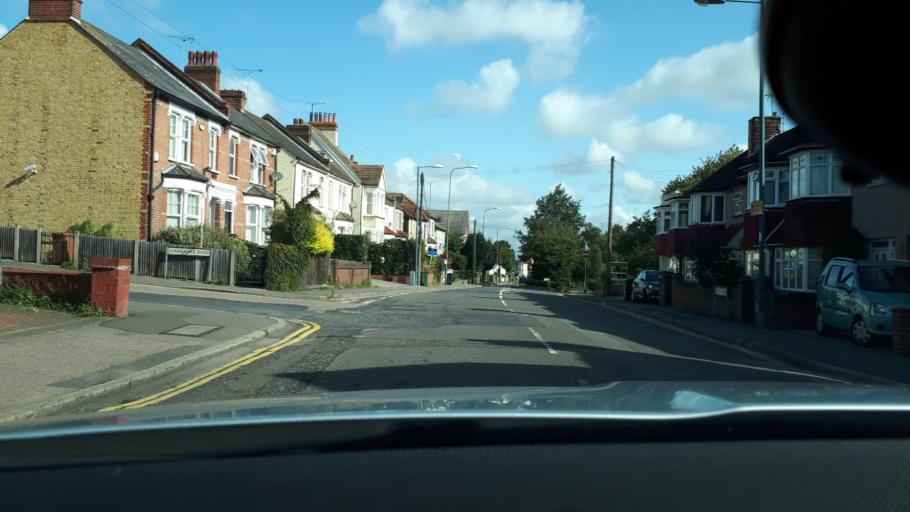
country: GB
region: England
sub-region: Kent
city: Dartford
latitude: 51.4423
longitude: 0.2122
